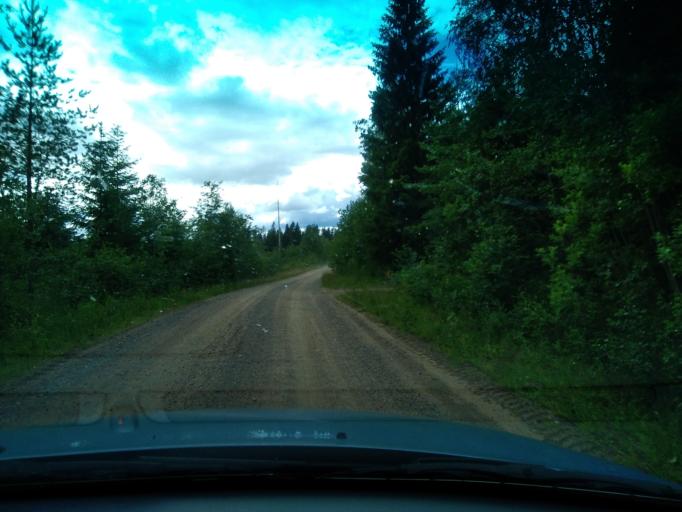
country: FI
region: Central Finland
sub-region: Saarijaervi-Viitasaari
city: Karstula
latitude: 62.7871
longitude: 24.9464
